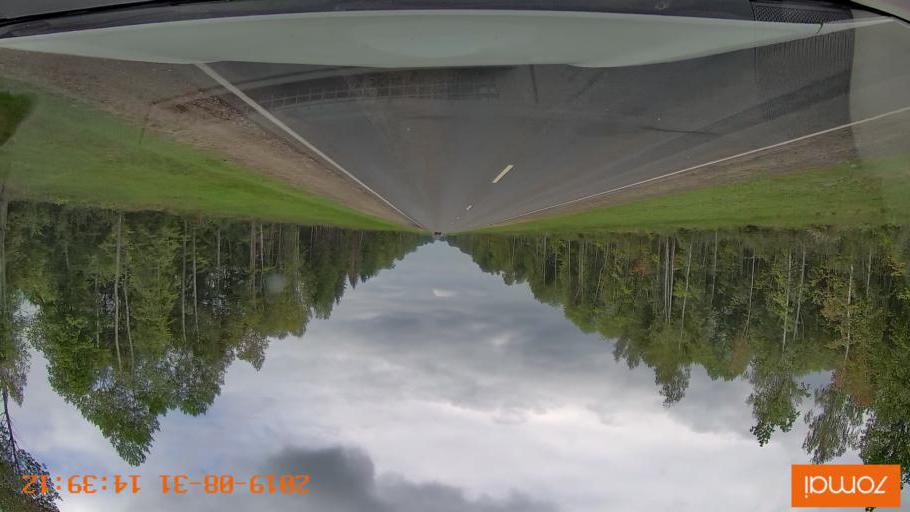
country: RU
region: Smolensk
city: Yekimovichi
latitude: 54.1900
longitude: 33.5470
